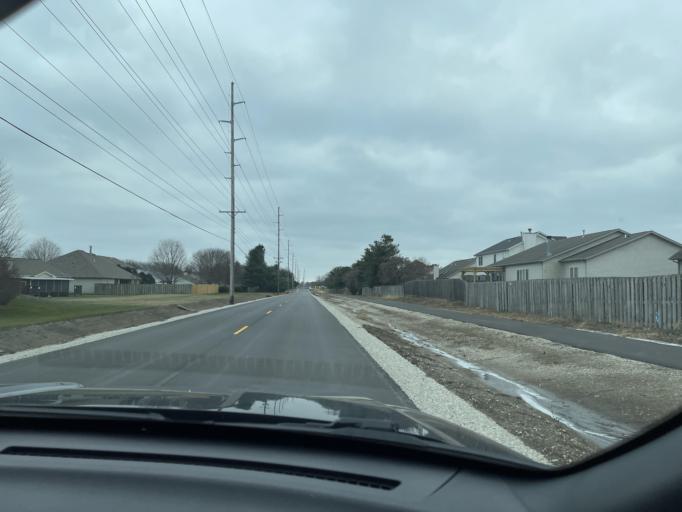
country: US
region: Illinois
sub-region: Sangamon County
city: Rochester
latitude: 39.7614
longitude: -89.5787
